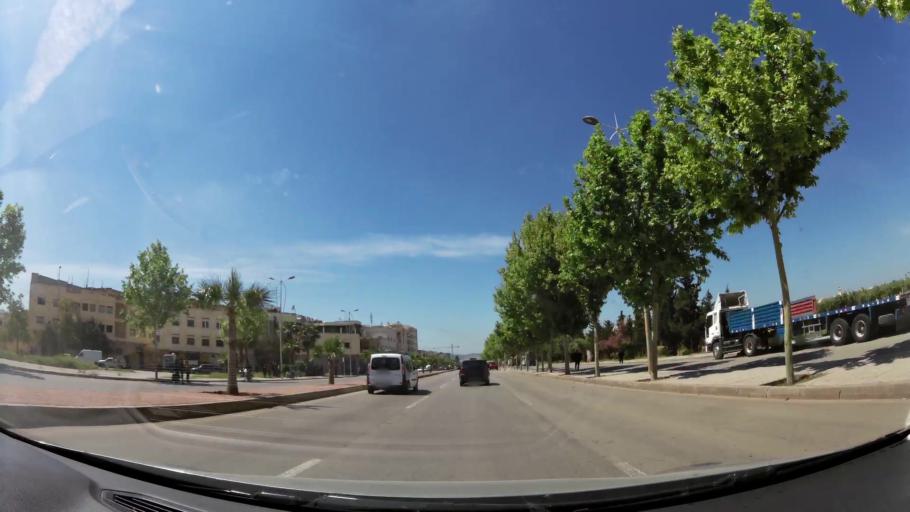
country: MA
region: Fes-Boulemane
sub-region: Fes
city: Fes
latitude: 34.0065
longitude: -4.9768
